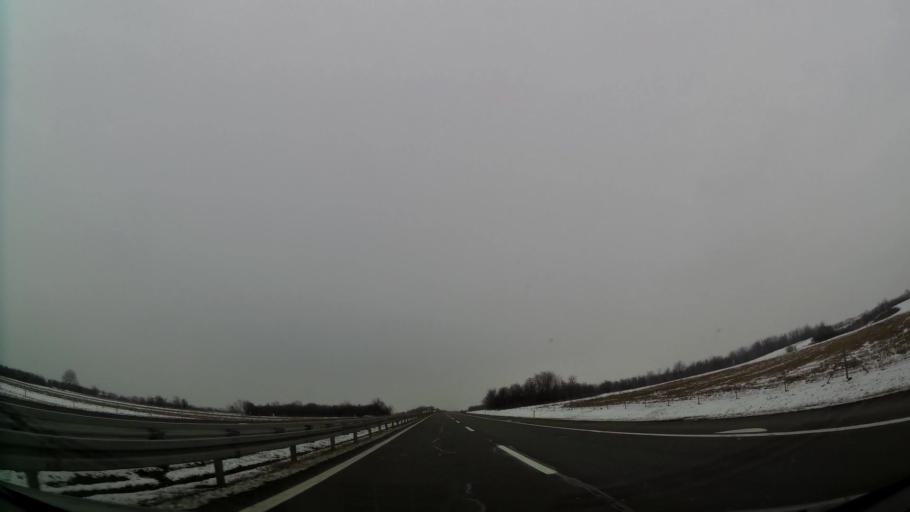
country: RS
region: Central Serbia
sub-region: Pomoravski Okrug
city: Cuprija
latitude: 43.8993
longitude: 21.3949
